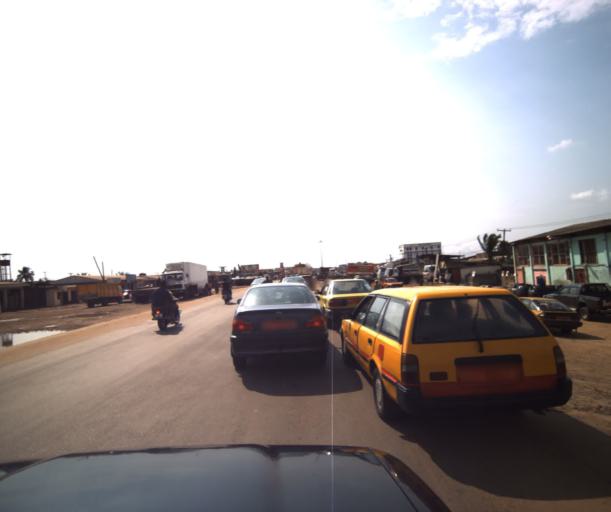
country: CM
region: Littoral
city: Douala
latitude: 4.0111
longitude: 9.7344
